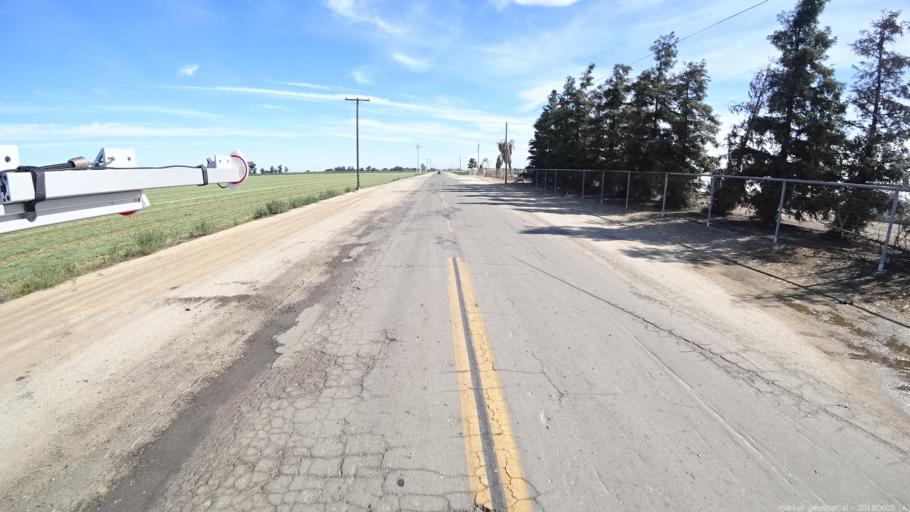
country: US
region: California
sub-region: Madera County
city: Chowchilla
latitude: 37.1351
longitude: -120.2927
